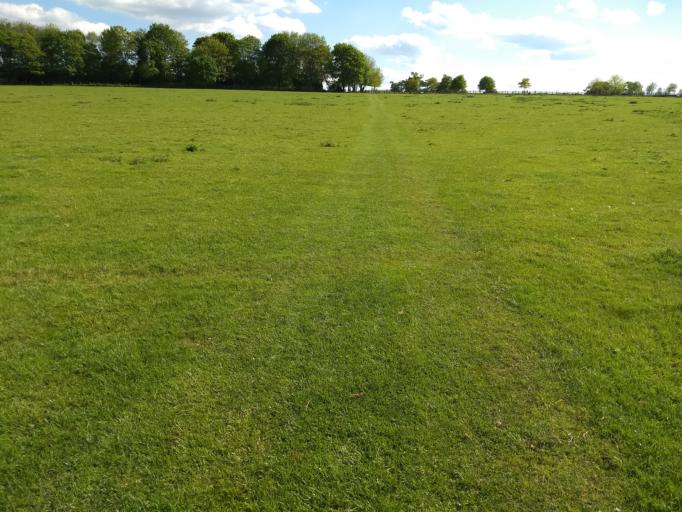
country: GB
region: England
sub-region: Milton Keynes
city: Castlethorpe
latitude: 52.0700
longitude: -0.8205
